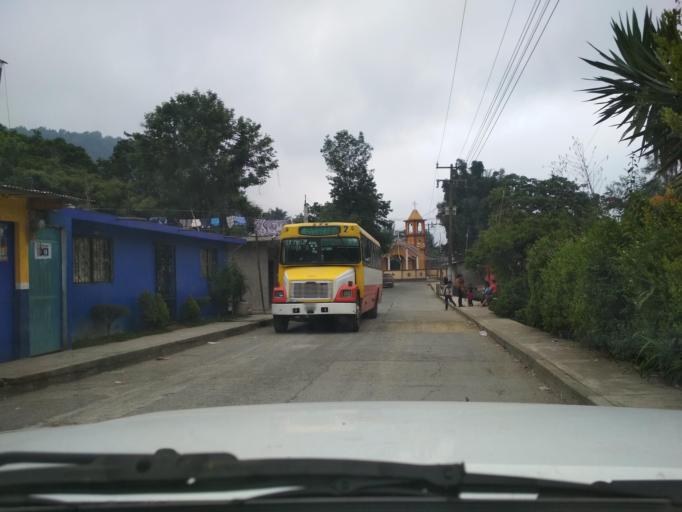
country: MX
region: Veracruz
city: La Perla
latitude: 18.9333
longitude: -97.1419
